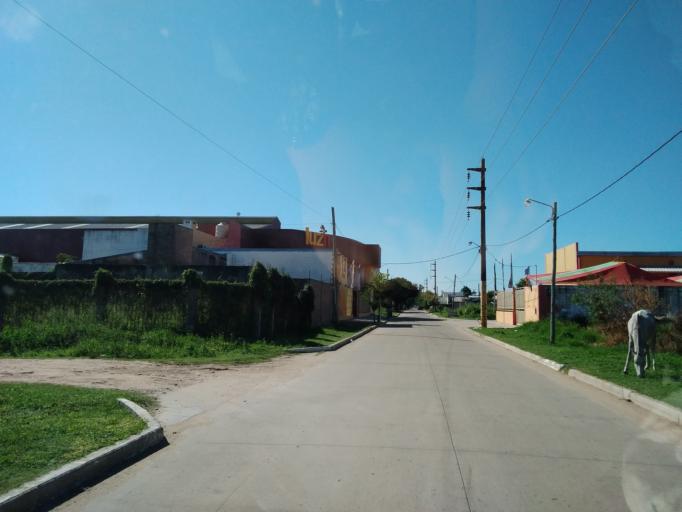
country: AR
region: Corrientes
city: Corrientes
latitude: -27.4722
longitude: -58.7929
